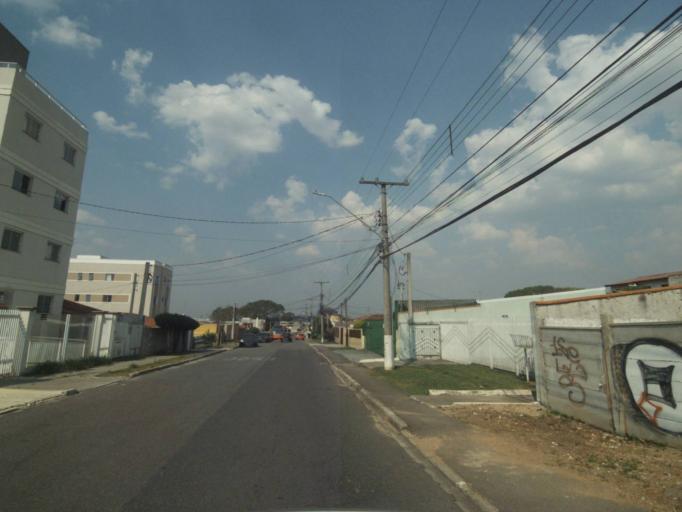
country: BR
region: Parana
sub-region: Sao Jose Dos Pinhais
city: Sao Jose dos Pinhais
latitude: -25.5359
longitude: -49.2389
